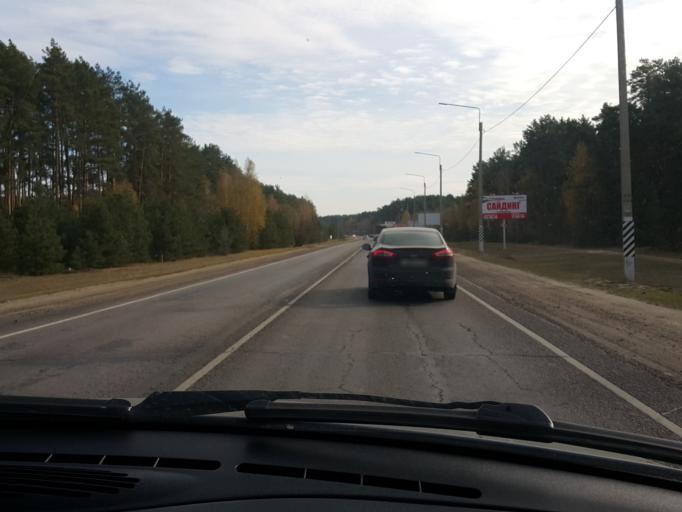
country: RU
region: Tambov
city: Donskoye
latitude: 52.7121
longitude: 41.5228
